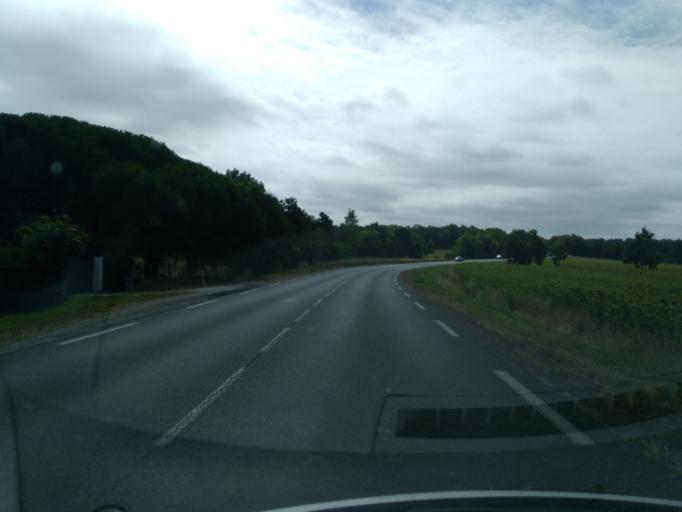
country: FR
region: Poitou-Charentes
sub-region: Departement de la Charente-Maritime
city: Breuillet
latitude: 45.7046
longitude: -1.0589
